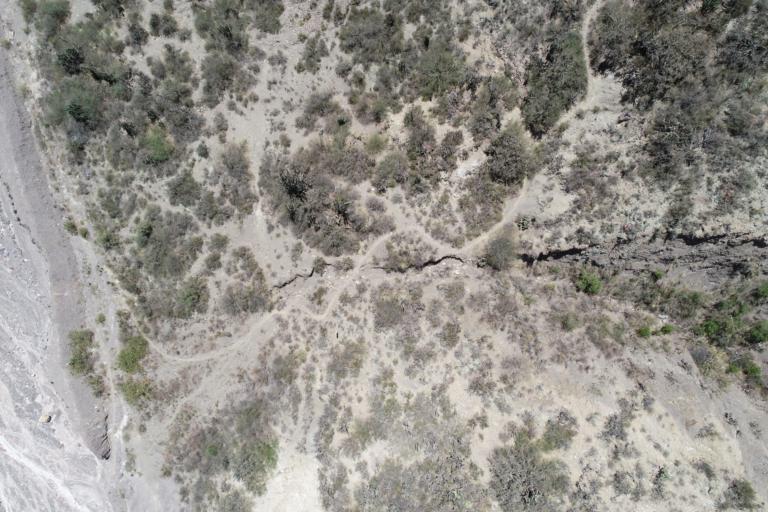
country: BO
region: La Paz
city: La Paz
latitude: -16.6434
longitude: -68.0395
